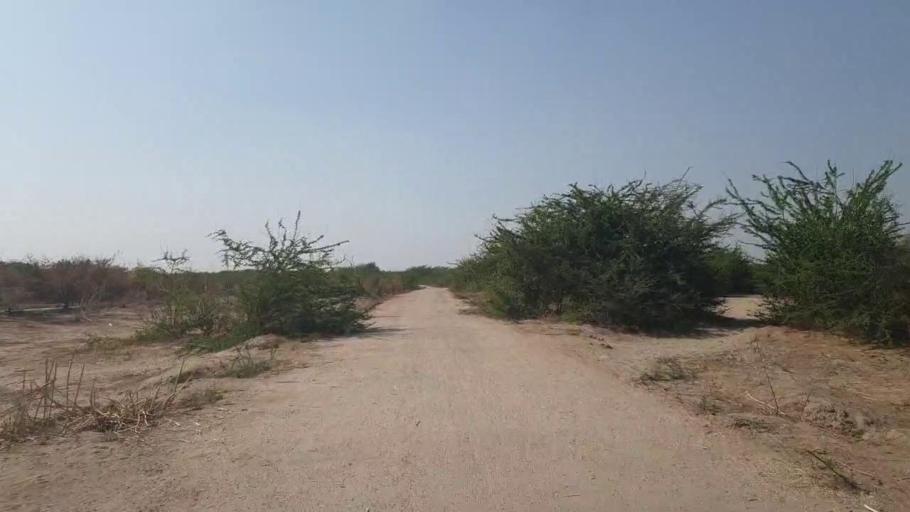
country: PK
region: Sindh
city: Dhoro Naro
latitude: 25.4978
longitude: 69.6251
